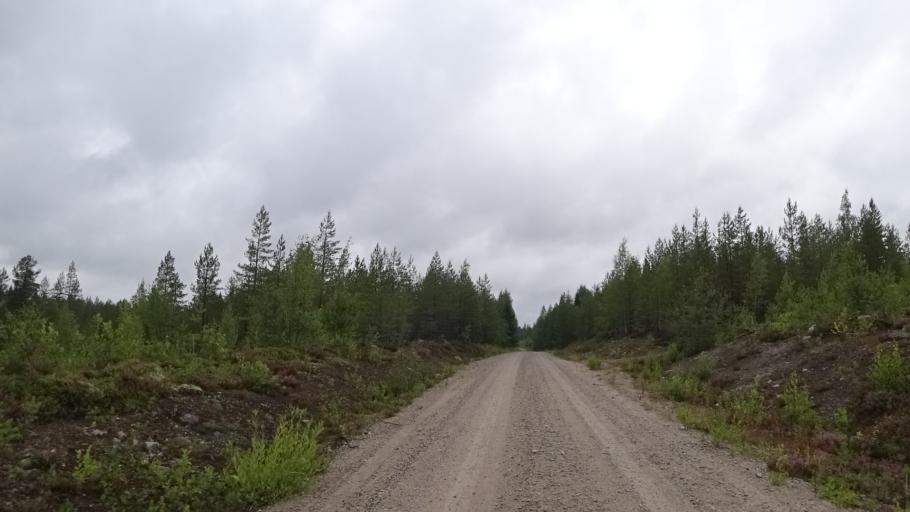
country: FI
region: North Karelia
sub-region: Pielisen Karjala
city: Lieksa
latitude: 63.5054
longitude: 30.1577
